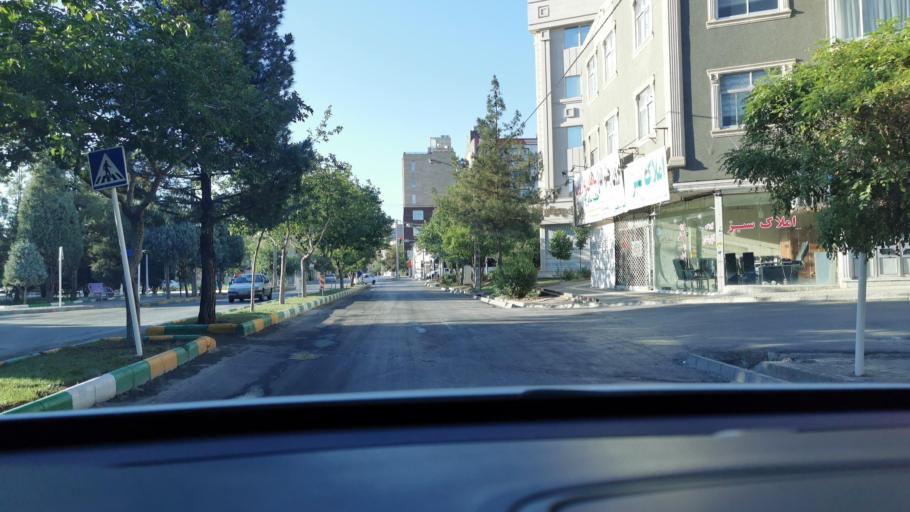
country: IR
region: Razavi Khorasan
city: Mashhad
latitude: 36.3593
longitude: 59.4909
